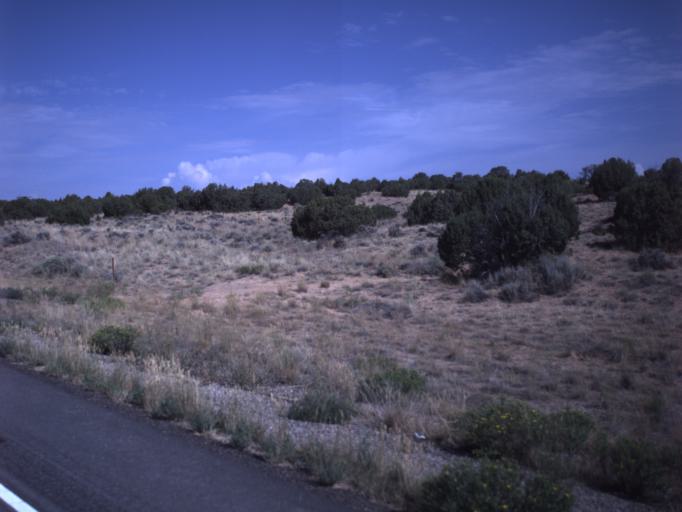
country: US
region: Utah
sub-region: Uintah County
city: Naples
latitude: 40.3209
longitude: -109.2562
